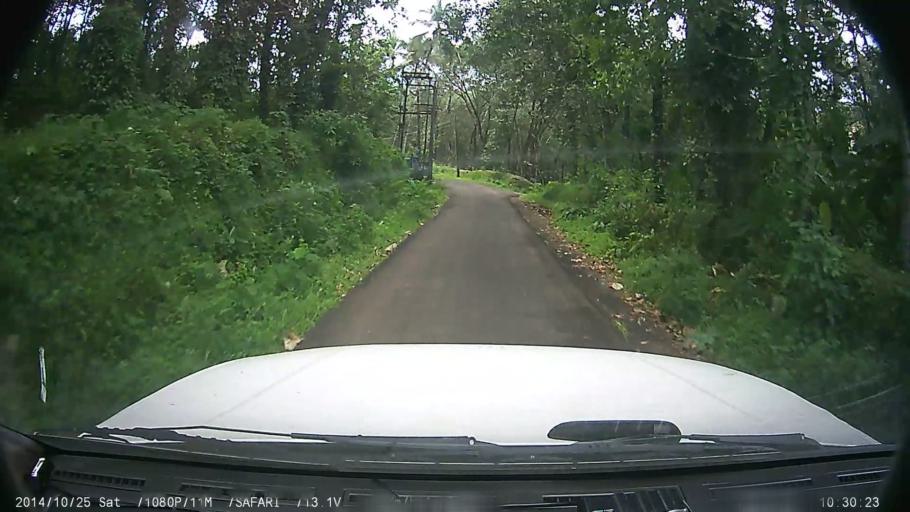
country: IN
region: Kerala
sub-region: Ernakulam
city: Muvattupuzha
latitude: 9.9246
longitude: 76.5678
